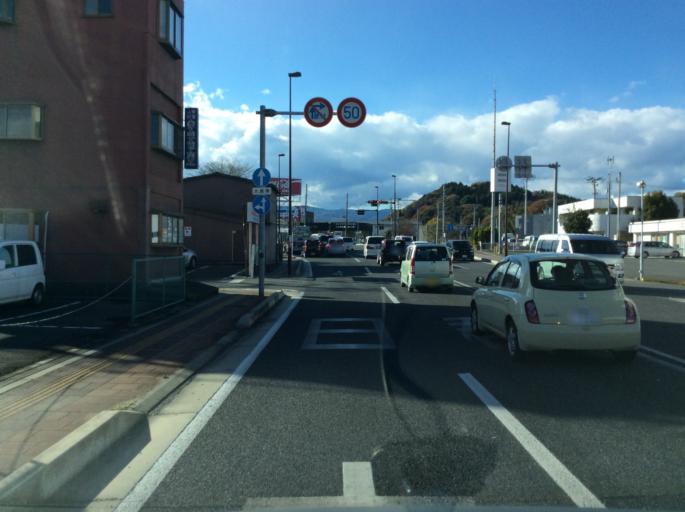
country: JP
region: Fukushima
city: Iwaki
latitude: 37.0532
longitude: 140.8809
